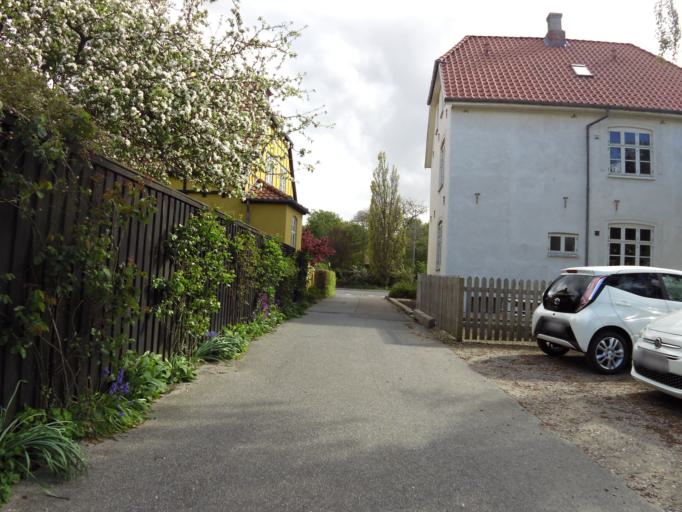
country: DK
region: South Denmark
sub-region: Esbjerg Kommune
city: Ribe
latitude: 55.3285
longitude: 8.7734
